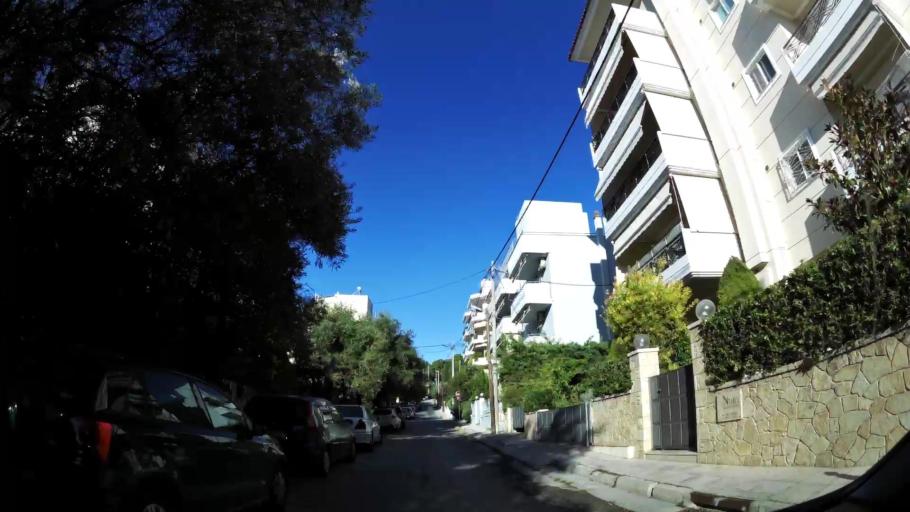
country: GR
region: Attica
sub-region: Nomarchia Anatolikis Attikis
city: Pallini
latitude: 38.0006
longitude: 23.8754
